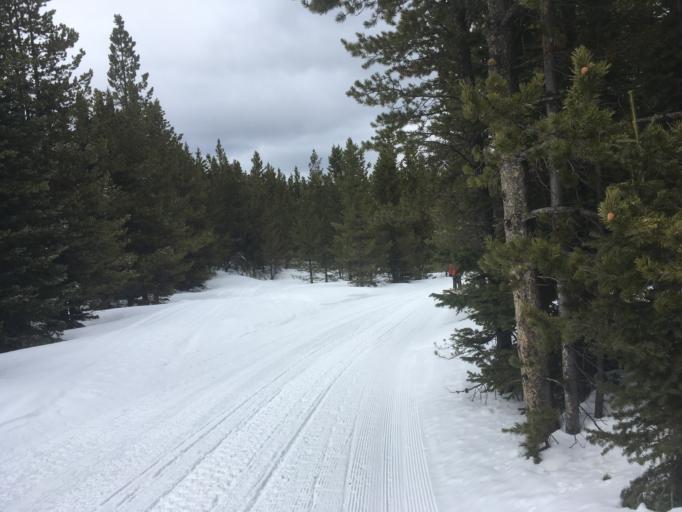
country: US
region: Montana
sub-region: Meagher County
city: White Sulphur Springs
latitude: 46.8502
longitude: -110.7020
